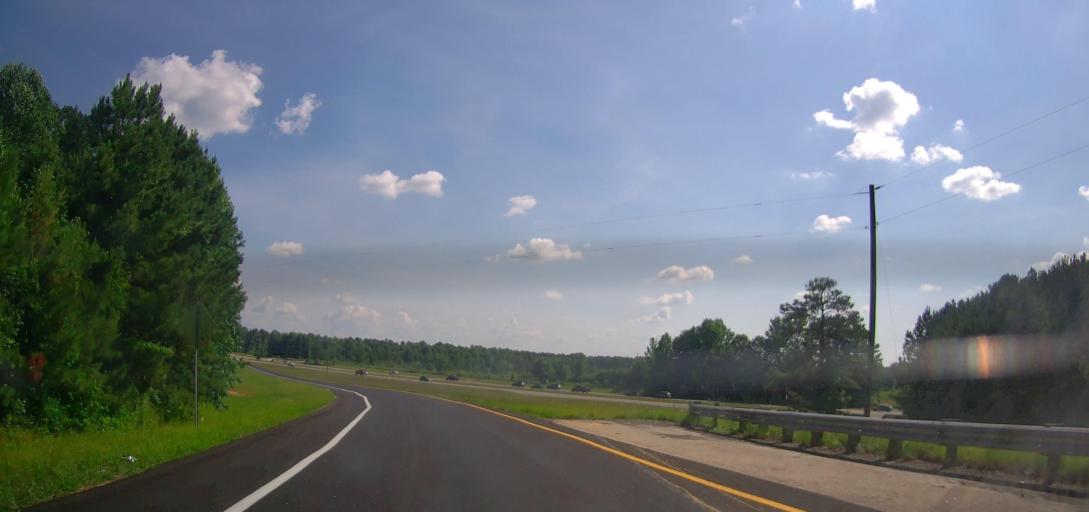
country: US
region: Georgia
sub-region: Henry County
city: Hampton
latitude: 33.3742
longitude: -84.2958
